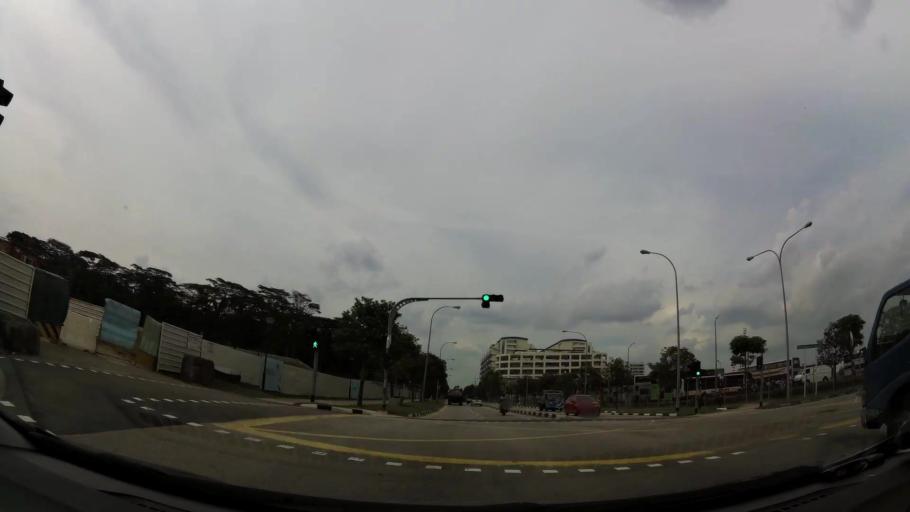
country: MY
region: Johor
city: Johor Bahru
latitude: 1.4471
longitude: 103.7920
